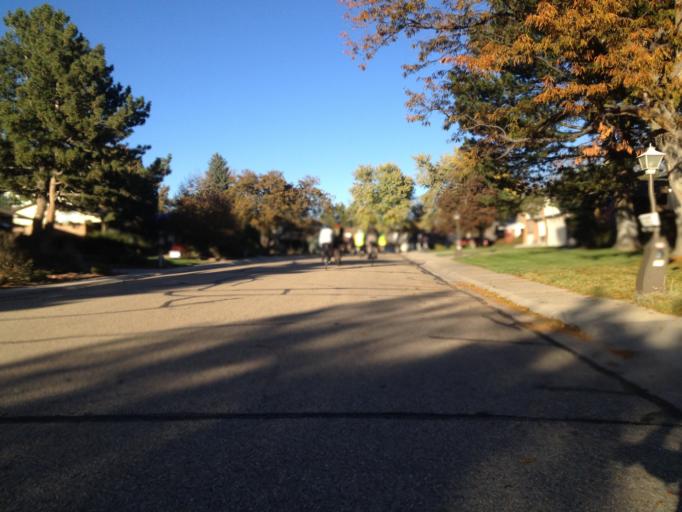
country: US
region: Colorado
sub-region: Boulder County
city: Longmont
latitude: 40.1847
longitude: -105.1445
